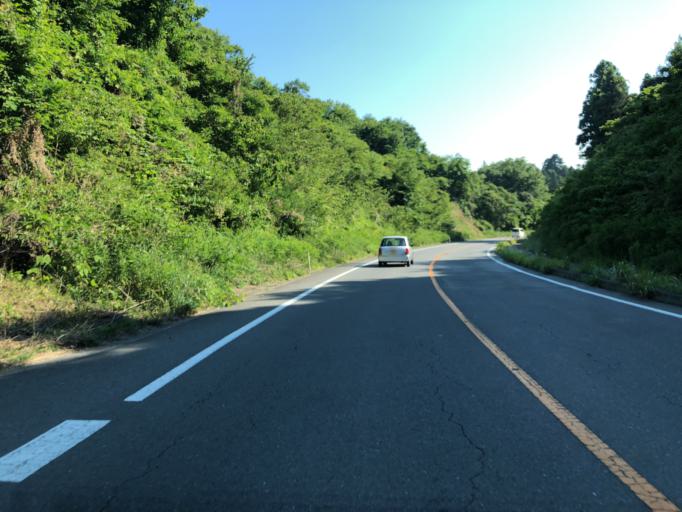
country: JP
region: Fukushima
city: Iwaki
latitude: 36.9459
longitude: 140.8246
